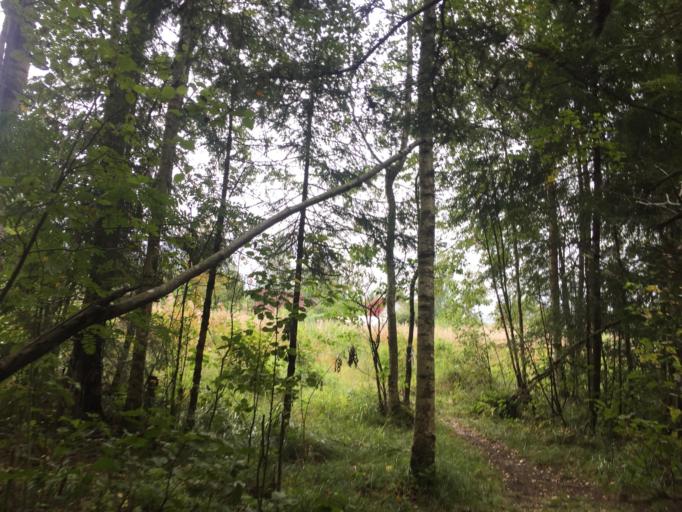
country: RU
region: Leningrad
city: Rozhdestveno
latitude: 59.2936
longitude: 30.0117
